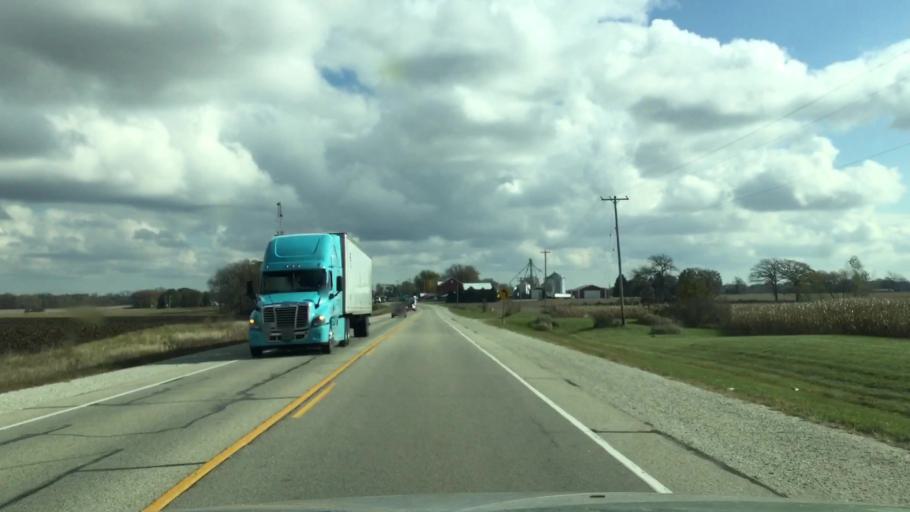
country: US
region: Wisconsin
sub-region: Racine County
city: Eagle Lake
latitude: 42.7414
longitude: -88.1202
